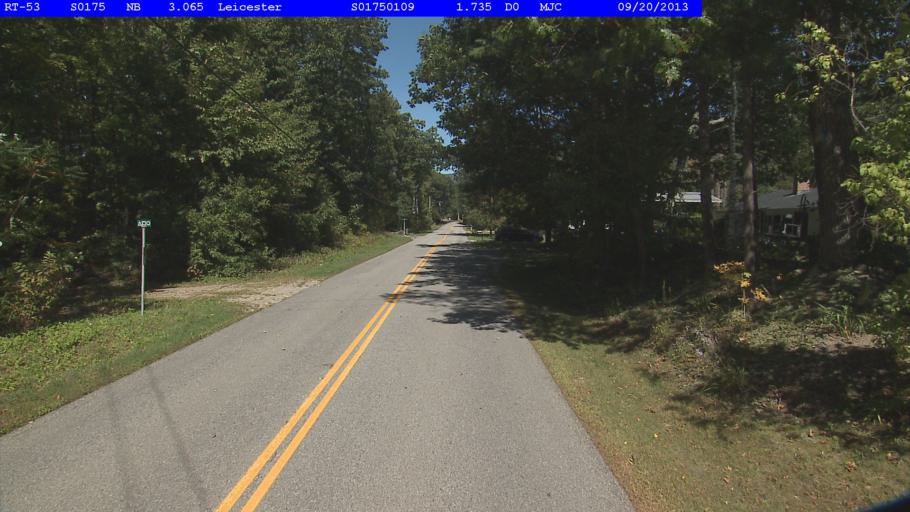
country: US
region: Vermont
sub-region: Rutland County
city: Brandon
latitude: 43.8679
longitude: -73.0654
